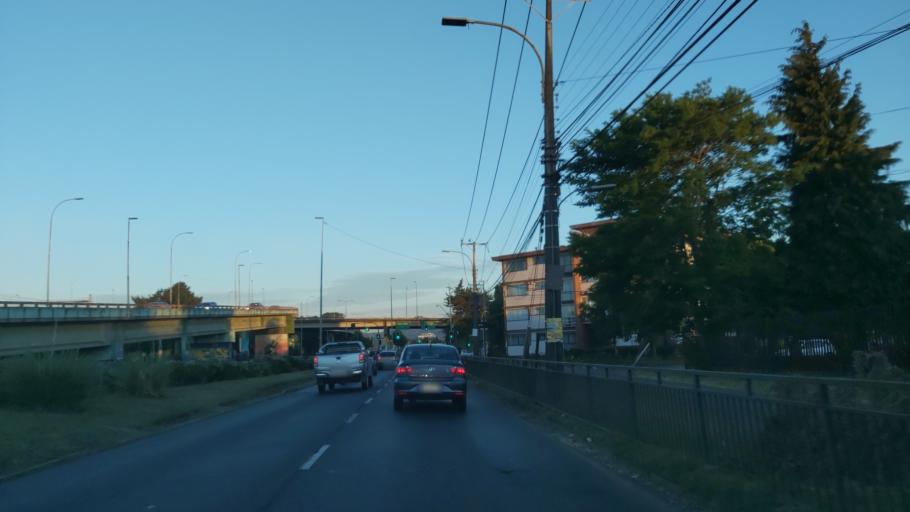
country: CL
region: Biobio
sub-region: Provincia de Concepcion
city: Concepcion
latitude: -36.8386
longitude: -73.1029
